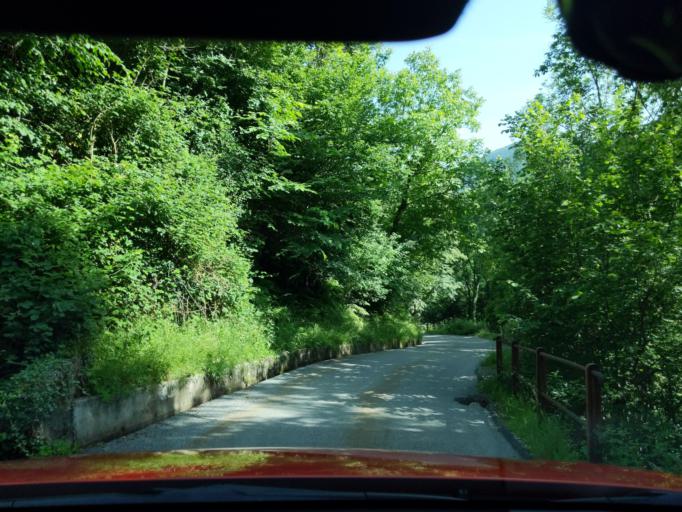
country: IT
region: Piedmont
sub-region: Provincia Verbano-Cusio-Ossola
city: Falmenta
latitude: 46.0891
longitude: 8.5972
